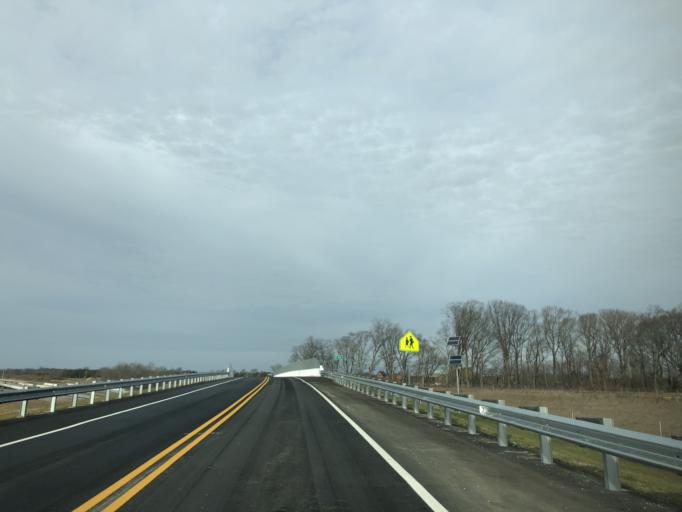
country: US
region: Delaware
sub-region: New Castle County
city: Delaware City
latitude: 39.5236
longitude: -75.6617
